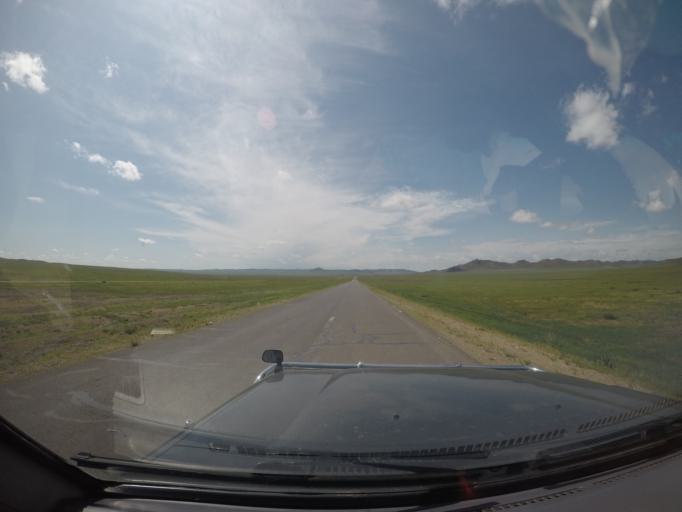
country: MN
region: Hentiy
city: Moron
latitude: 47.3814
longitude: 110.4463
